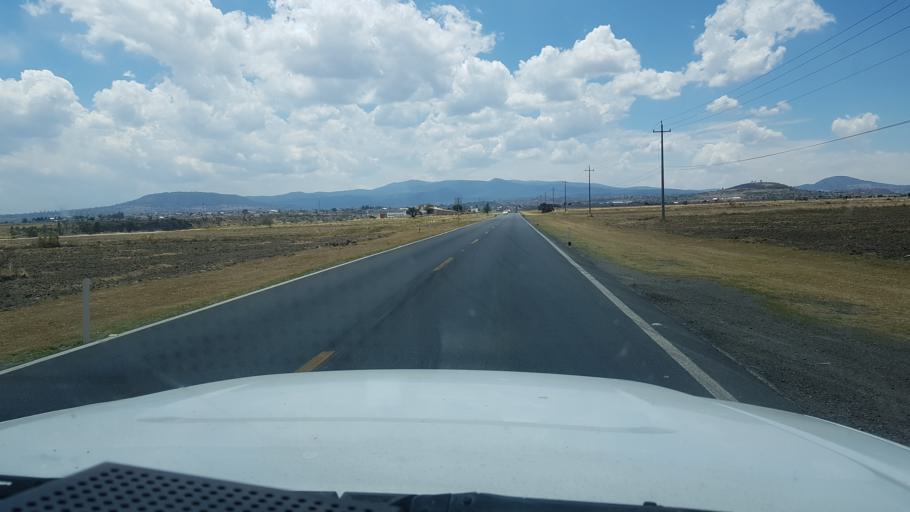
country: MX
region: Hidalgo
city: Calpulalpan
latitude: 19.6115
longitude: -98.5577
